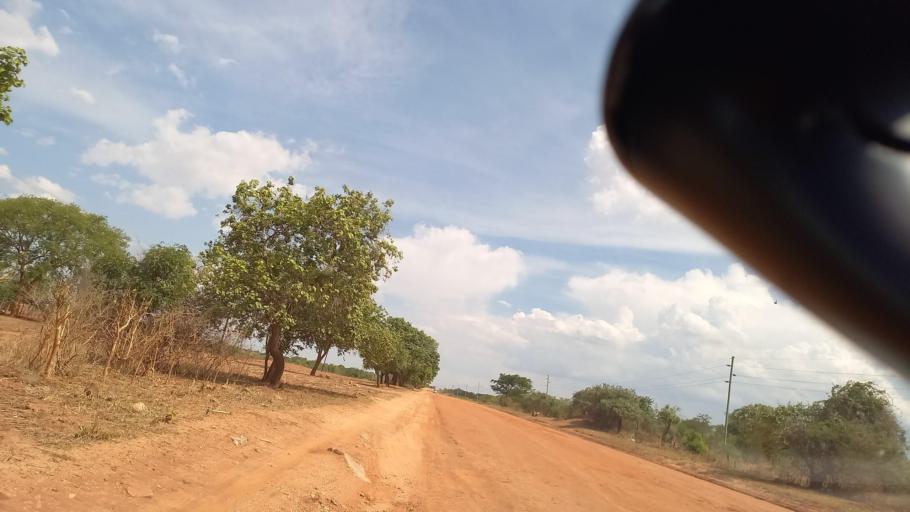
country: ZM
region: Lusaka
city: Kafue
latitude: -16.1372
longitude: 28.0513
